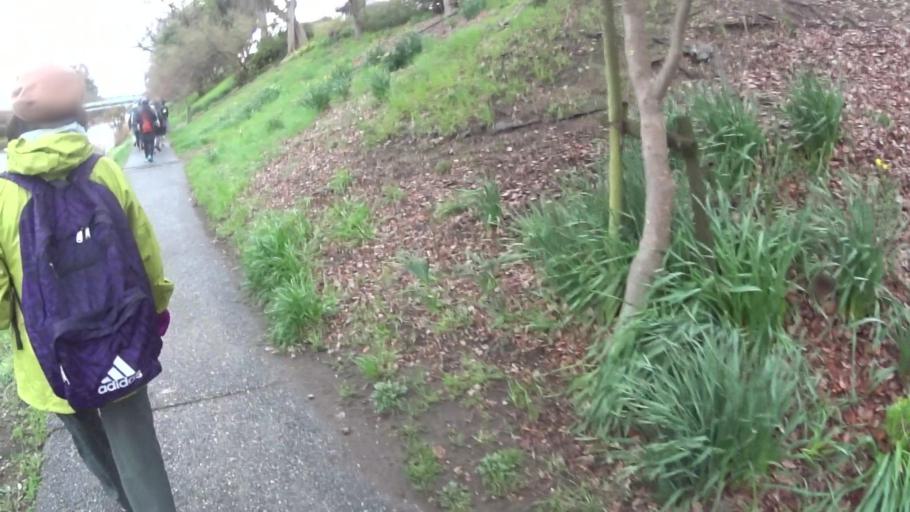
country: JP
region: Kyoto
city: Uji
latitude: 34.9290
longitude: 135.7556
